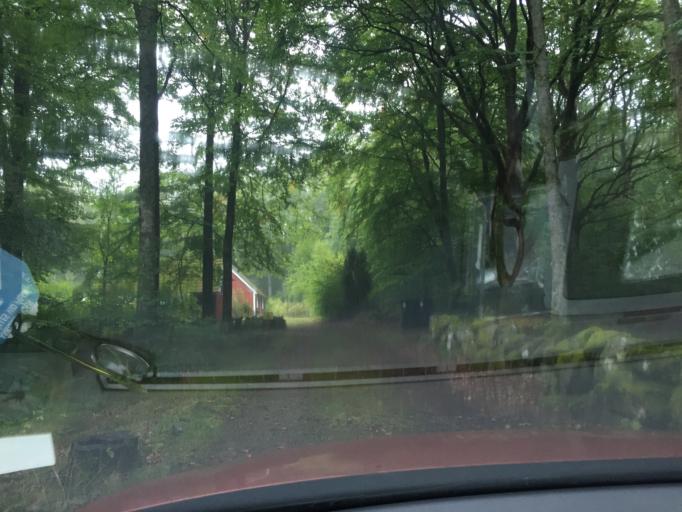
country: SE
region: Skane
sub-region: Osby Kommun
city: Osby
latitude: 56.3526
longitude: 13.9699
